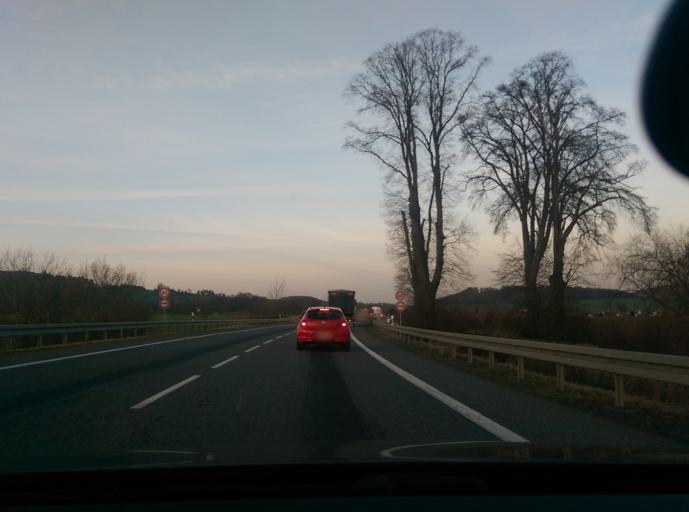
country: DE
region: Thuringia
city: Hohengandern
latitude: 51.3804
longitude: 9.9080
